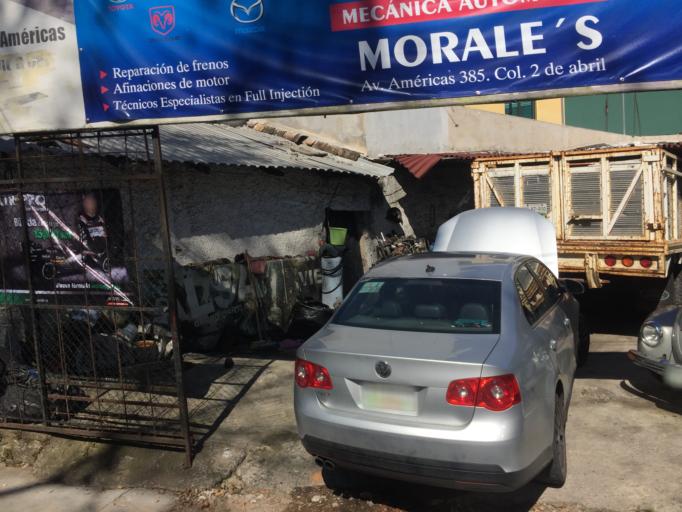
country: MX
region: Veracruz
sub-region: Xalapa
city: Xalapa de Enriquez
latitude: 19.5345
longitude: -96.9096
